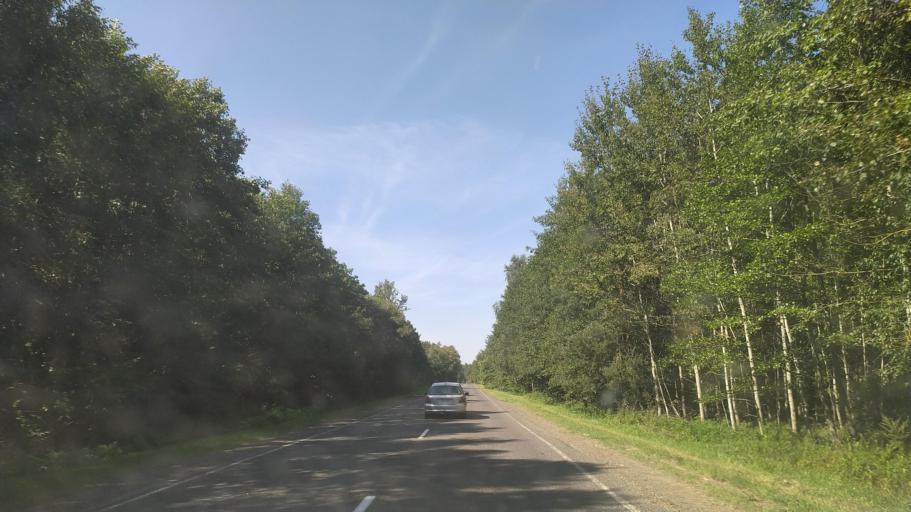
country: BY
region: Brest
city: Byaroza
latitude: 52.4094
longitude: 24.9950
